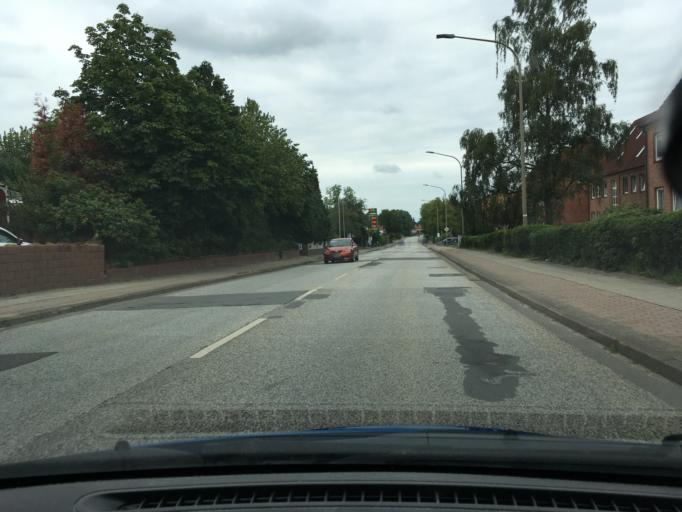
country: DE
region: Schleswig-Holstein
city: Geesthacht
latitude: 53.4498
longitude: 10.3594
